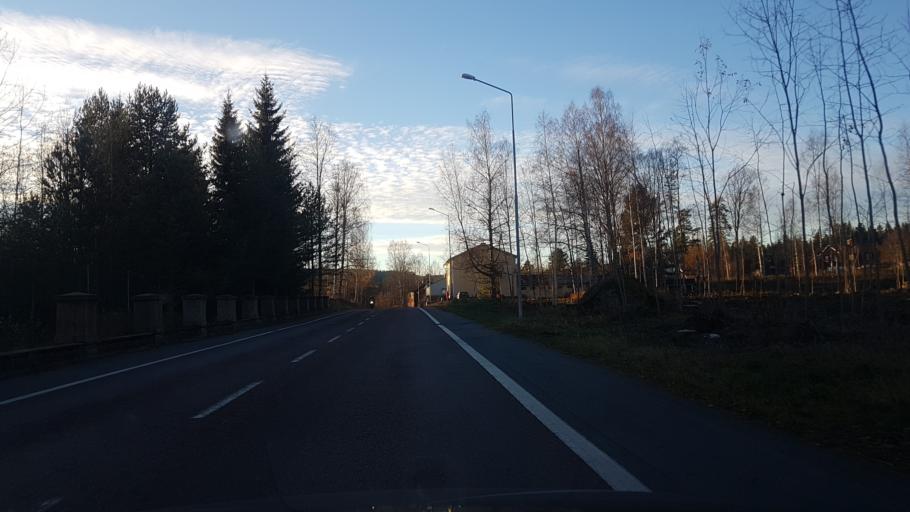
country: SE
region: Dalarna
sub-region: Faluns Kommun
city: Bjursas
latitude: 60.7137
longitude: 15.2948
